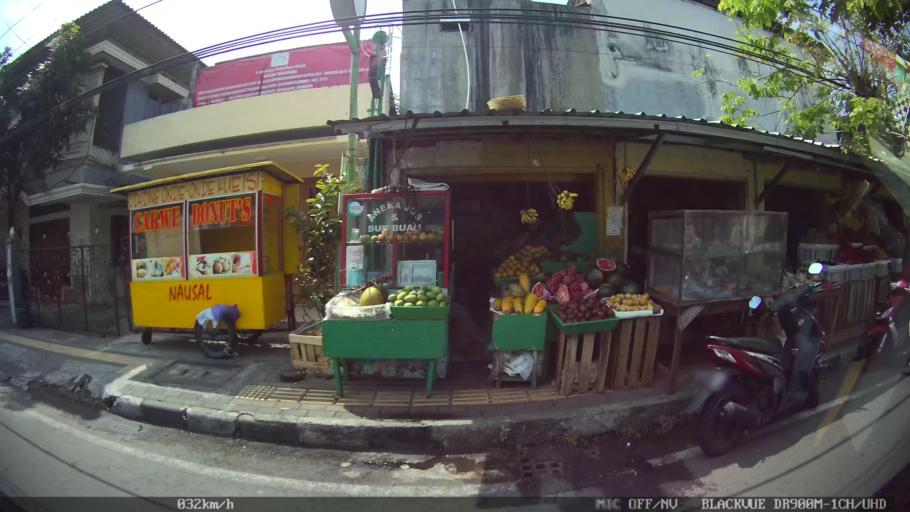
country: ID
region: Daerah Istimewa Yogyakarta
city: Yogyakarta
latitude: -7.8087
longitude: 110.3877
